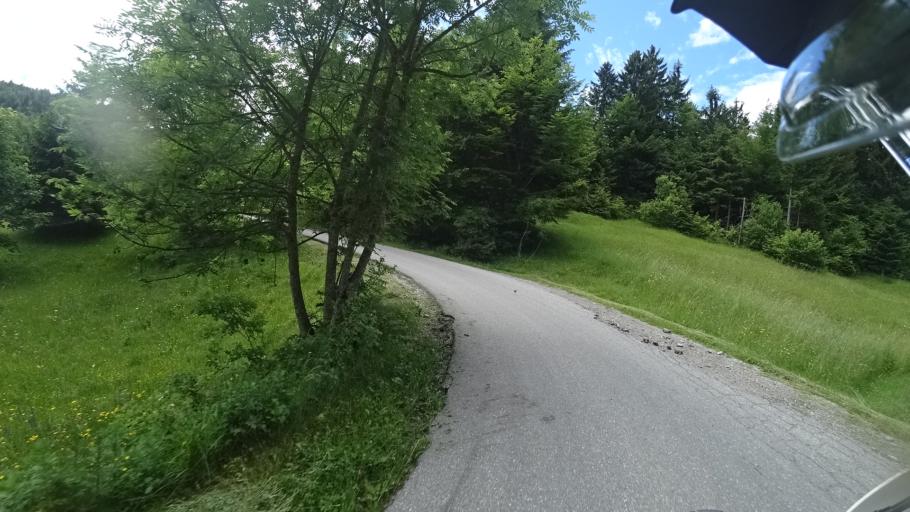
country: SI
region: Loski Potok
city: Hrib-Loski Potok
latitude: 45.6149
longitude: 14.5835
